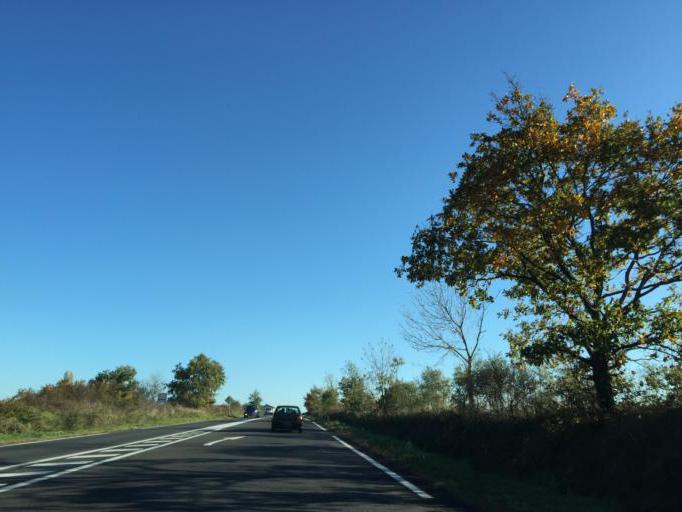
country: FR
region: Rhone-Alpes
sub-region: Departement du Rhone
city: Saint-Andeol-le-Chateau
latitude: 45.6062
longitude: 4.6918
